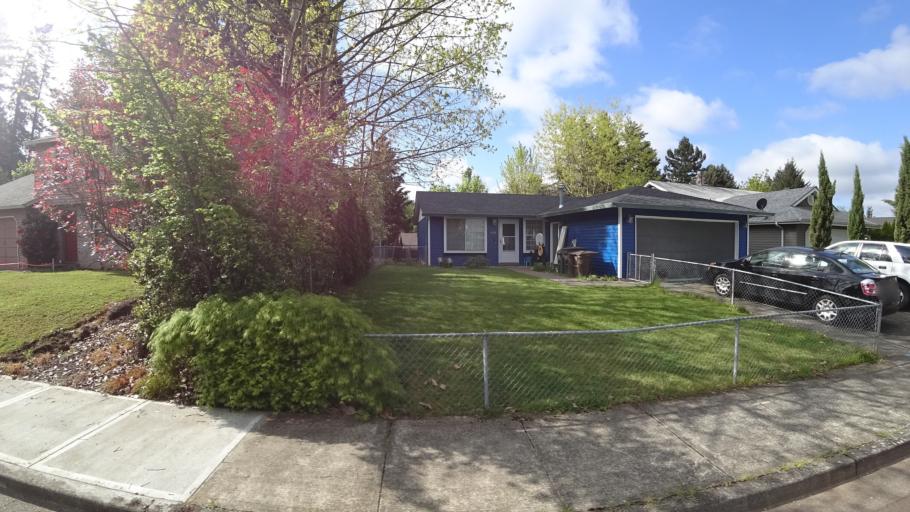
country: US
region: Oregon
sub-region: Washington County
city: Hillsboro
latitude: 45.5137
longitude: -122.9801
